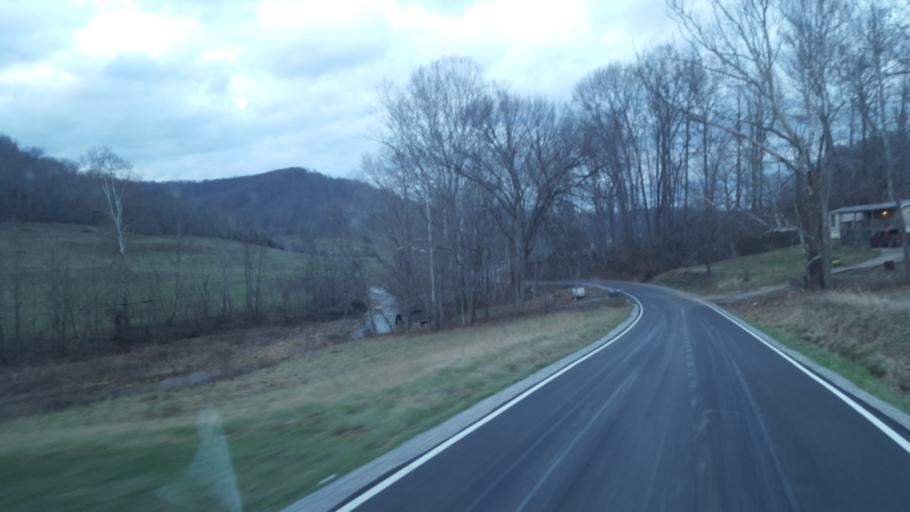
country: US
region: Kentucky
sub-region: Lewis County
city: Vanceburg
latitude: 38.5206
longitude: -83.4748
